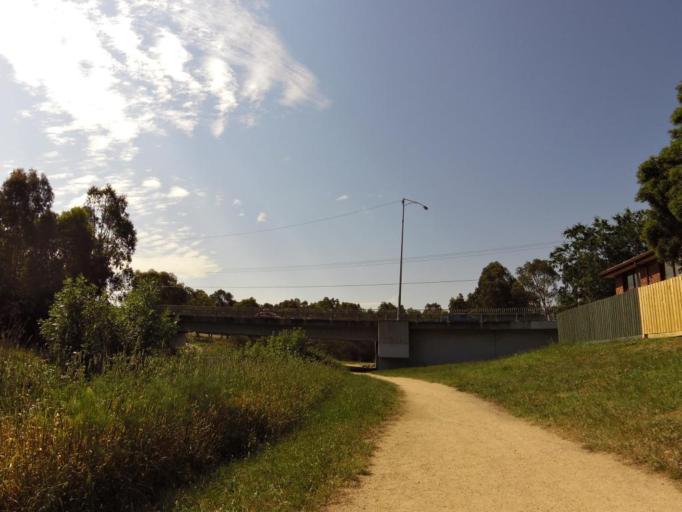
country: AU
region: Victoria
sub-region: Whittlesea
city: Epping
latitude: -37.6455
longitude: 145.0319
